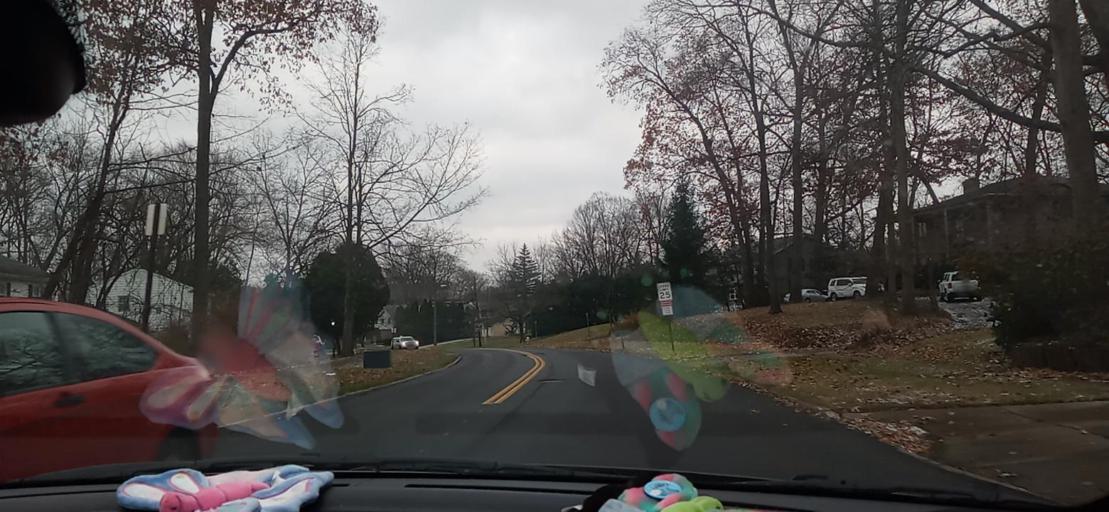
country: US
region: Ohio
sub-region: Summit County
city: Fairlawn
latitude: 41.1224
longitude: -81.5753
